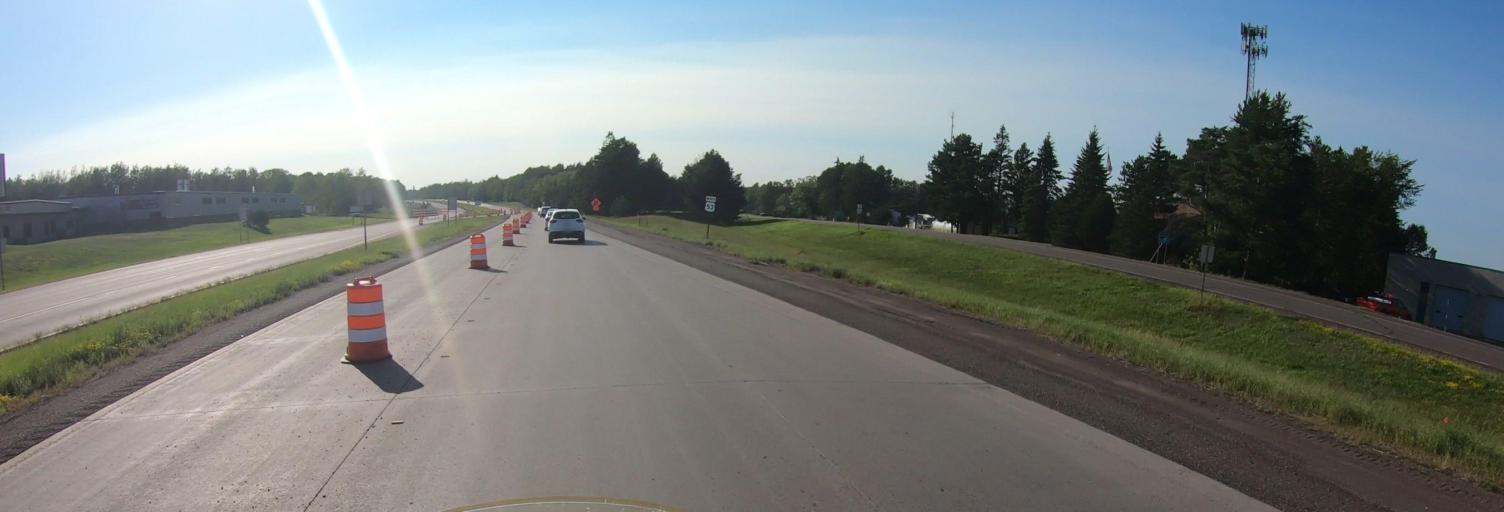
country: US
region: Minnesota
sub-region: Saint Louis County
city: Hermantown
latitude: 46.8509
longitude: -92.2851
